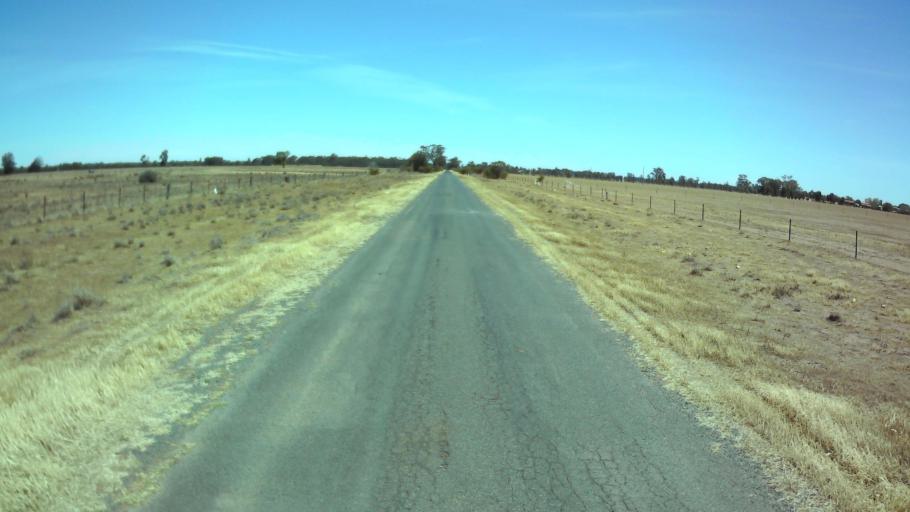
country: AU
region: New South Wales
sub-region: Weddin
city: Grenfell
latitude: -33.8905
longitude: 147.6883
